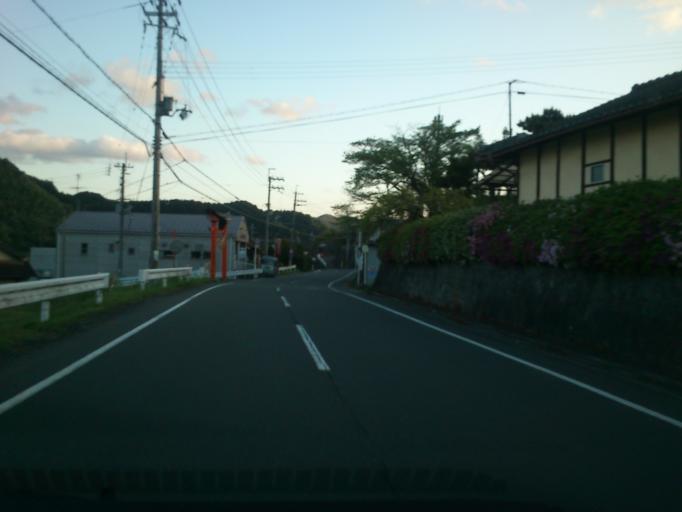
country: JP
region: Kyoto
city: Ayabe
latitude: 35.1869
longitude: 135.4139
